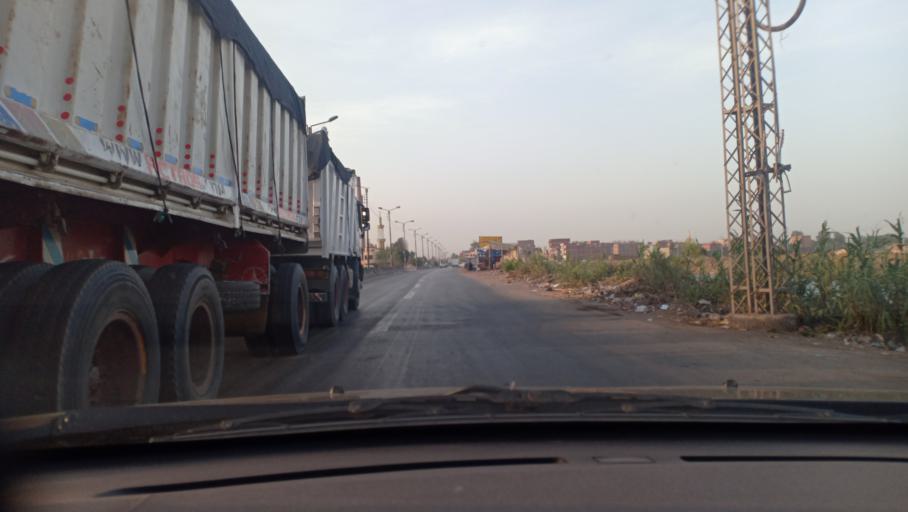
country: EG
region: Muhafazat al Gharbiyah
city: Zifta
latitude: 30.6093
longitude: 31.2755
